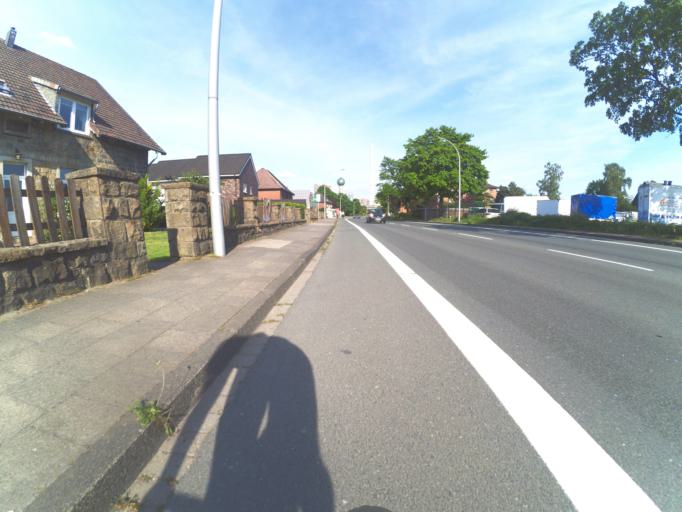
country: DE
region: North Rhine-Westphalia
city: Ibbenburen
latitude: 52.2879
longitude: 7.7296
